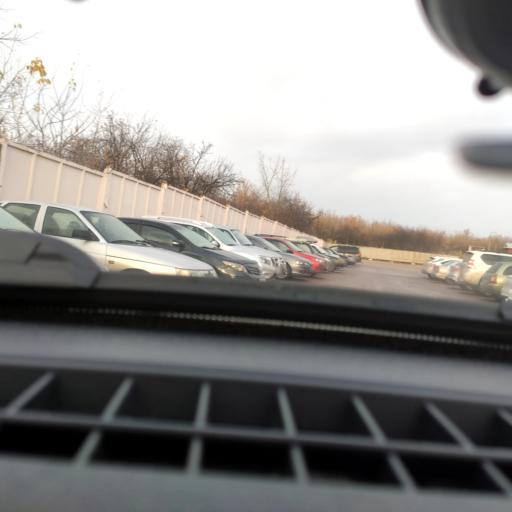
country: RU
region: Bashkortostan
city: Ufa
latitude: 54.8246
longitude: 56.1193
